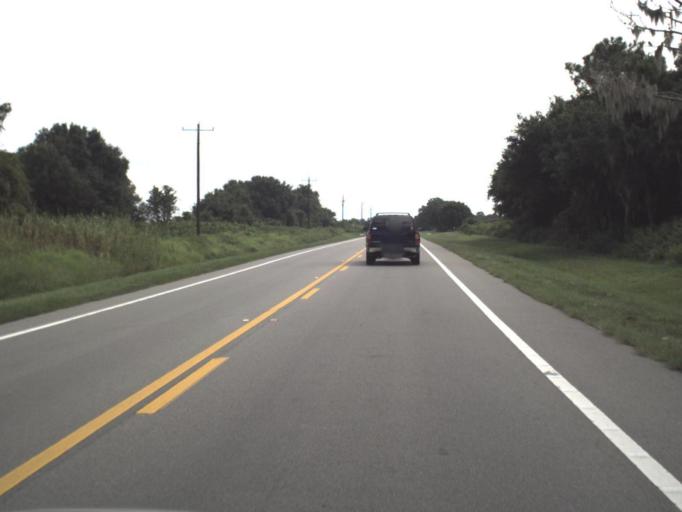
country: US
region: Florida
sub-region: Hillsborough County
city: Wimauma
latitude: 27.6004
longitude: -82.2956
